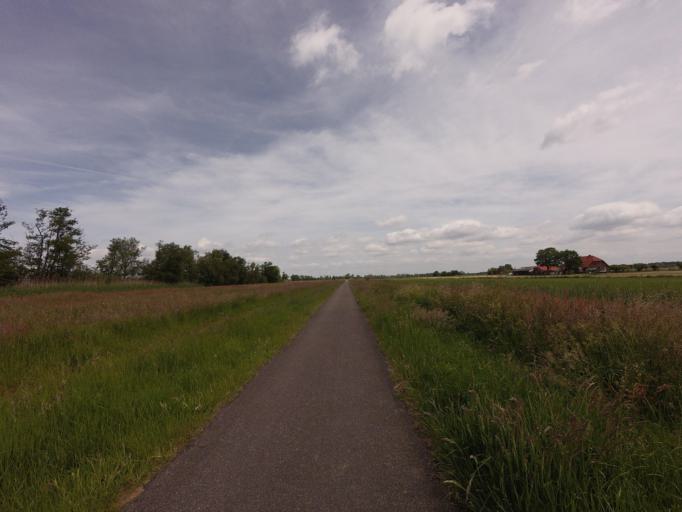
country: NL
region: Utrecht
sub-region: Gemeente Utrecht
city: Utrecht
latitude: 52.1316
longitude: 5.1319
